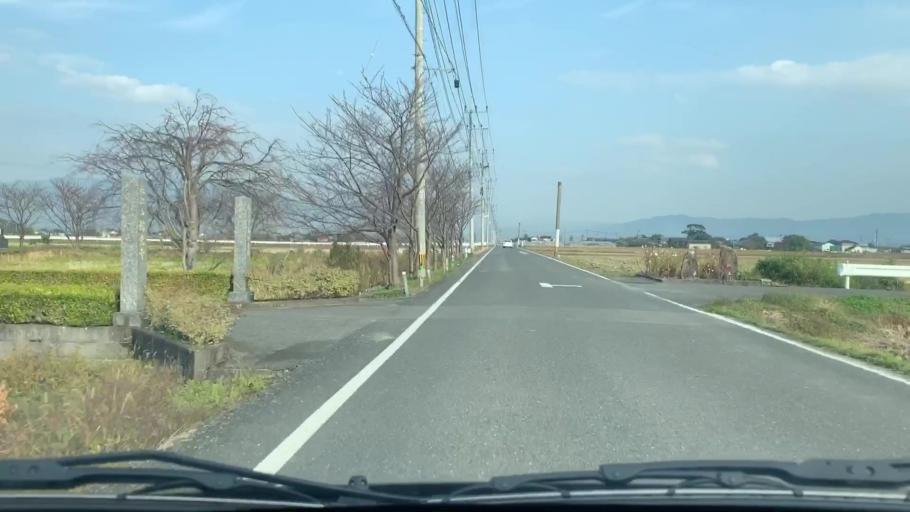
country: JP
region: Saga Prefecture
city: Saga-shi
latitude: 33.2492
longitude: 130.2582
